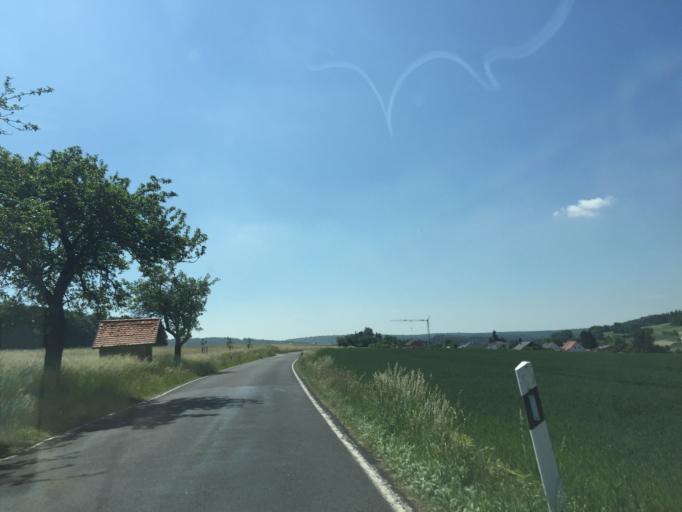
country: DE
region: Bavaria
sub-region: Regierungsbezirk Unterfranken
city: Eichenbuhl
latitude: 49.6428
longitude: 9.3163
